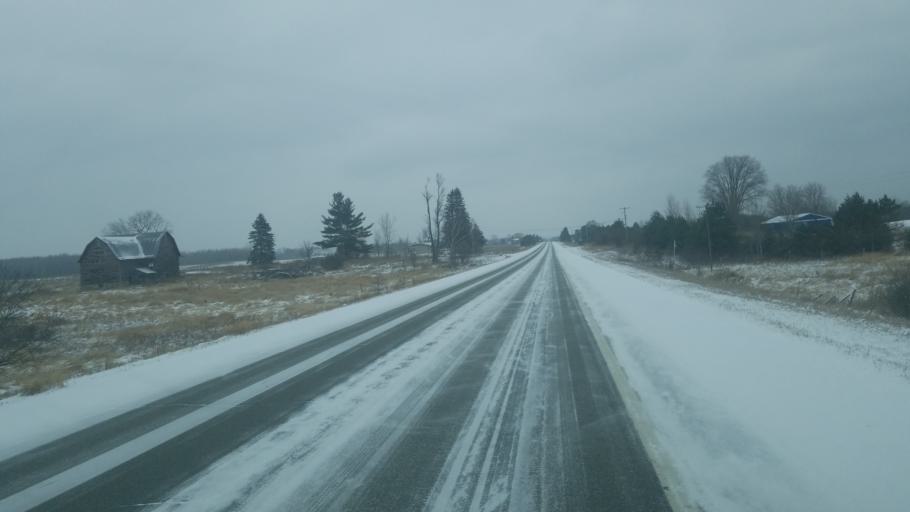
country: US
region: Michigan
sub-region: Osceola County
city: Evart
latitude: 43.9215
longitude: -85.1483
